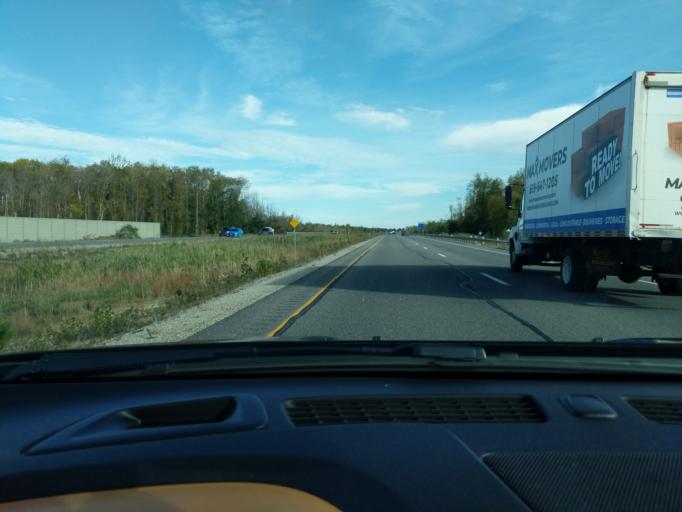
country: CA
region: Ontario
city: Collingwood
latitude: 44.4671
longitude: -80.1318
